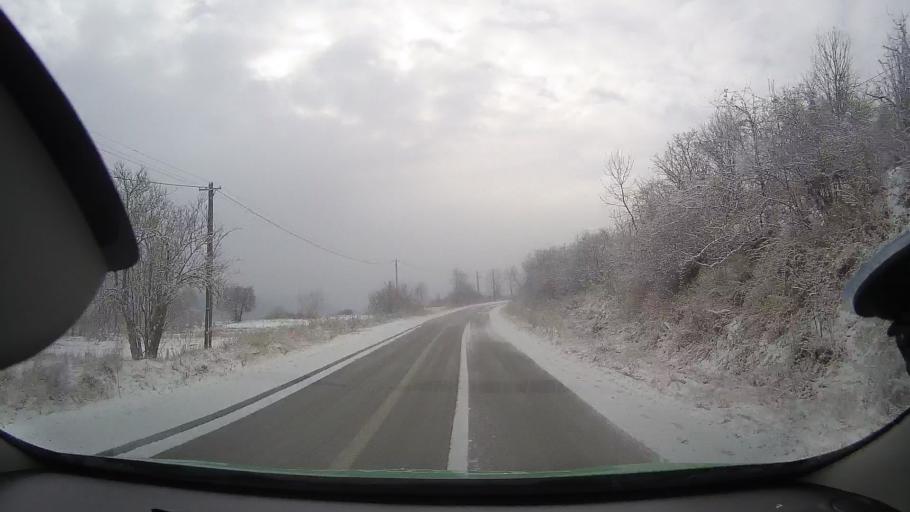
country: RO
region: Alba
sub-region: Comuna Rimetea
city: Rimetea
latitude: 46.4466
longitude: 23.5654
